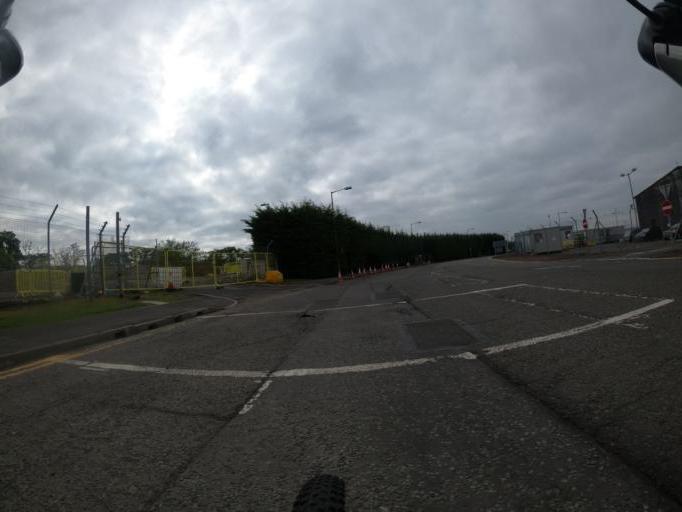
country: GB
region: Scotland
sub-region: Edinburgh
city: Ratho
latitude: 55.9435
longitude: -3.3556
